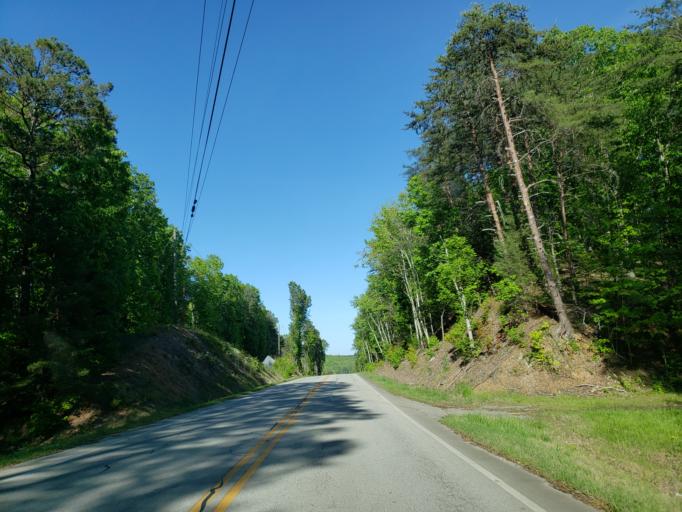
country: US
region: Georgia
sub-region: Polk County
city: Cedartown
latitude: 33.9092
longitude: -85.3085
